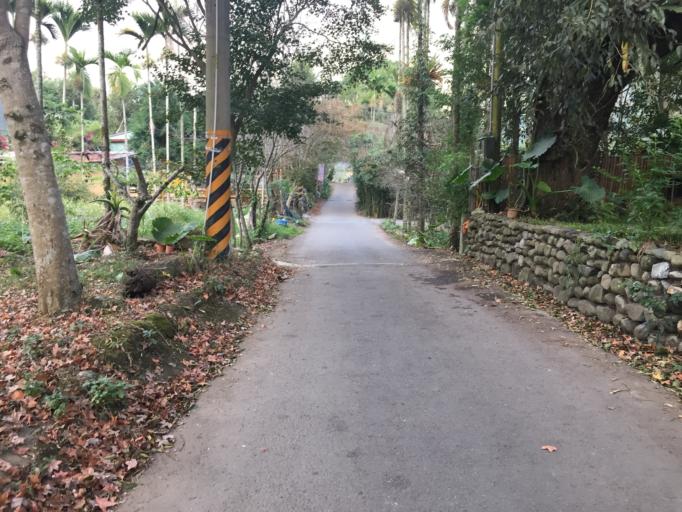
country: TW
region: Taiwan
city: Lugu
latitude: 23.6005
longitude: 120.8861
